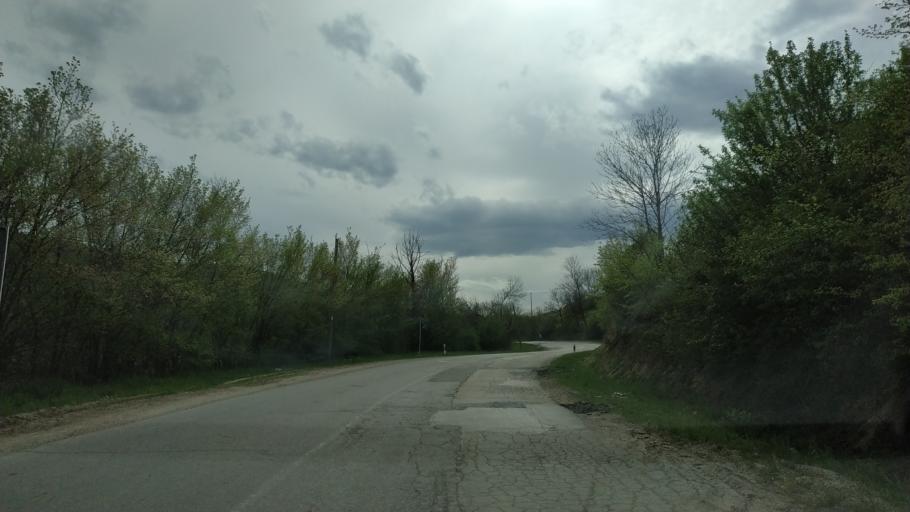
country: RS
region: Central Serbia
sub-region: Zajecarski Okrug
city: Soko Banja
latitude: 43.6442
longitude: 21.8957
